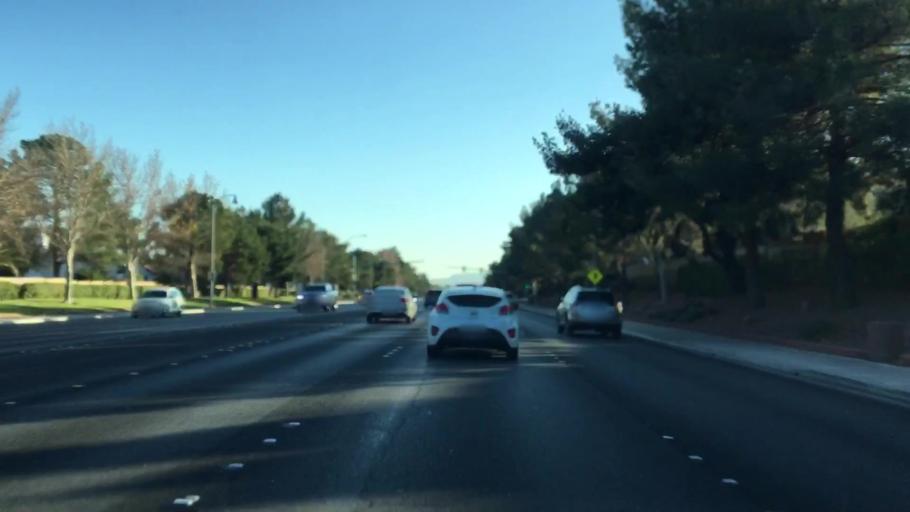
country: US
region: Nevada
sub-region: Clark County
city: Summerlin South
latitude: 36.1350
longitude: -115.2974
